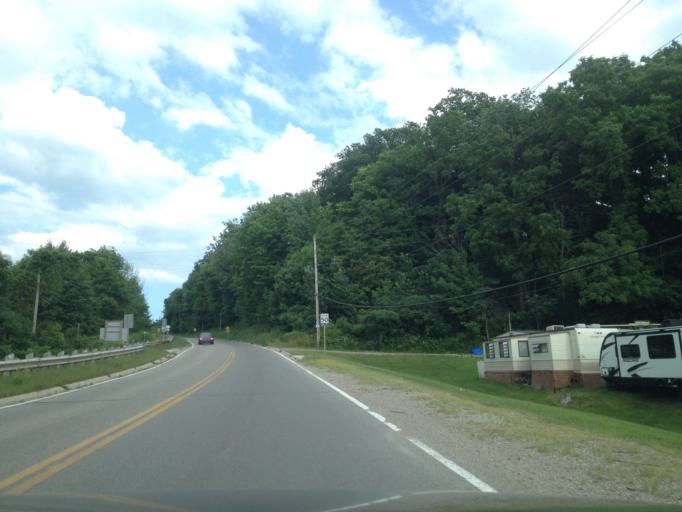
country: CA
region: Ontario
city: Aylmer
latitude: 42.6627
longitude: -81.0118
